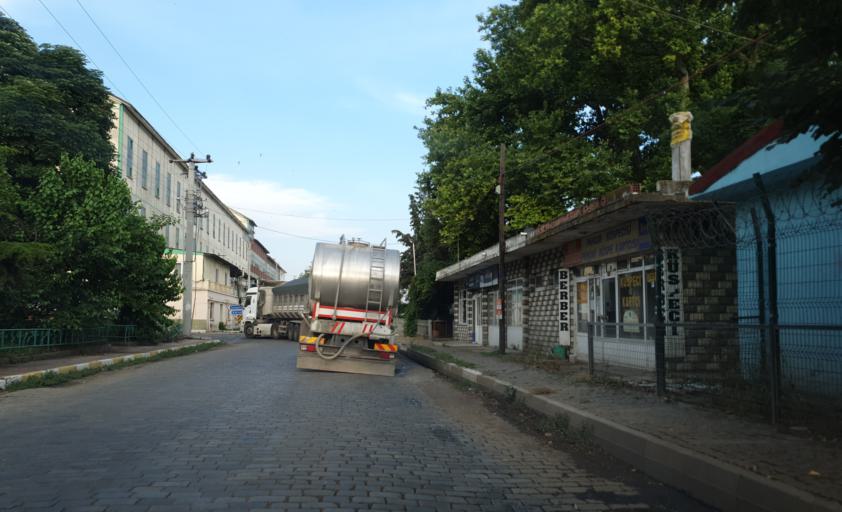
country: TR
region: Kirklareli
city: Babaeski
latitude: 41.3666
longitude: 27.1420
